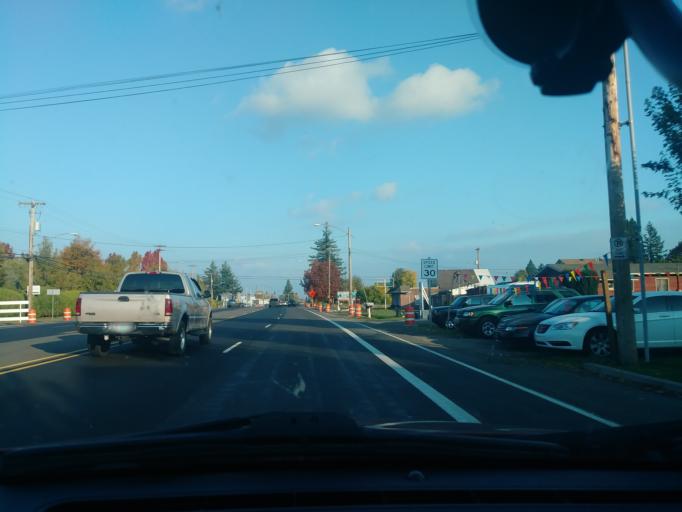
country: US
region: Oregon
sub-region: Washington County
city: Forest Grove
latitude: 45.5201
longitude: -123.0876
